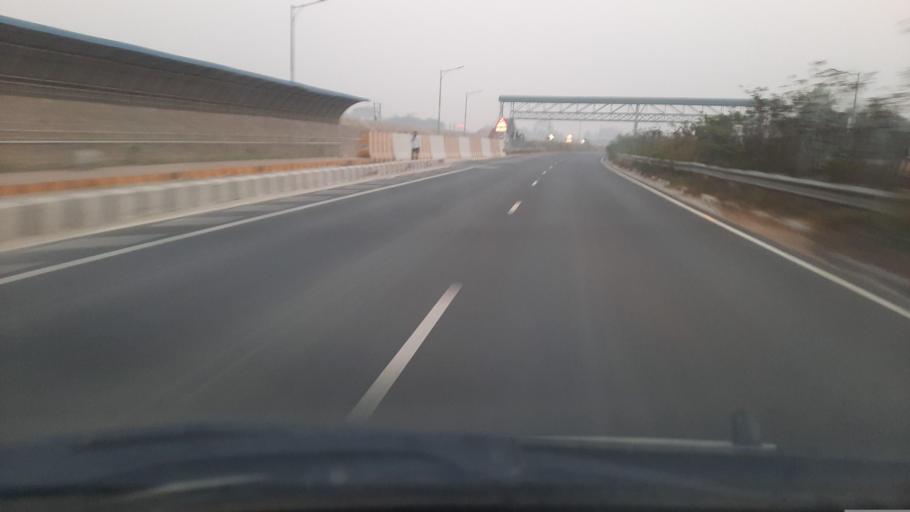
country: BD
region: Dhaka
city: Dohar
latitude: 23.5335
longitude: 90.2904
